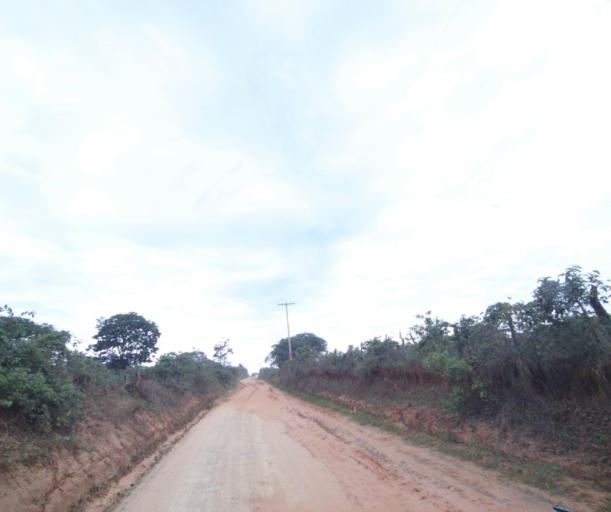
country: BR
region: Bahia
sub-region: Carinhanha
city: Carinhanha
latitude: -14.1808
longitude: -44.5169
